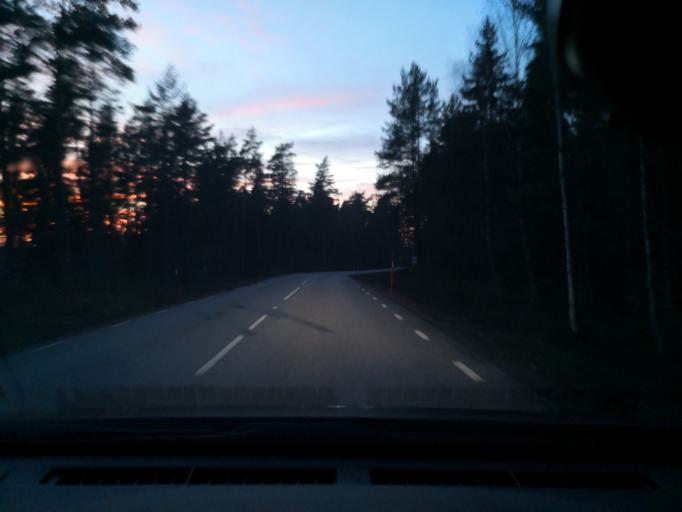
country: SE
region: OErebro
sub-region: Lindesbergs Kommun
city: Fellingsbro
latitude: 59.3997
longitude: 15.4776
